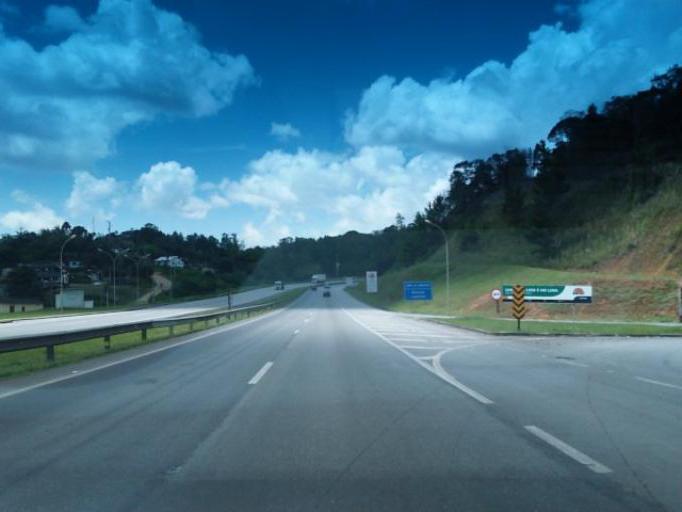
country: BR
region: Sao Paulo
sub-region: Juquitiba
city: Juquitiba
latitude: -24.0056
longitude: -47.1589
